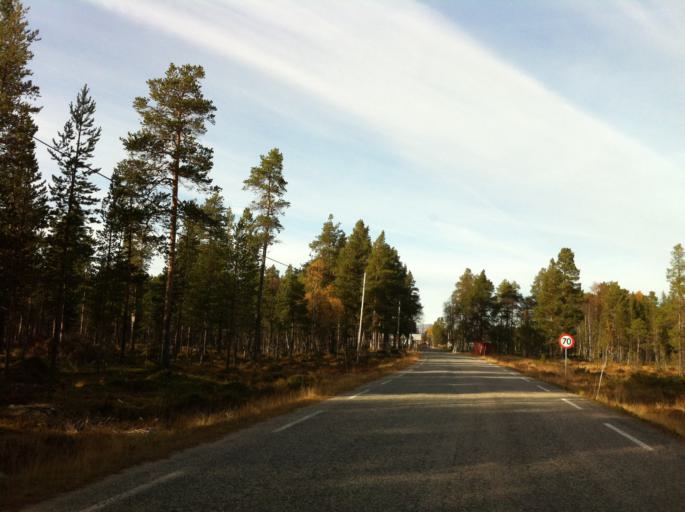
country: NO
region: Hedmark
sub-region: Engerdal
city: Engerdal
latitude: 62.1424
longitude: 11.9654
